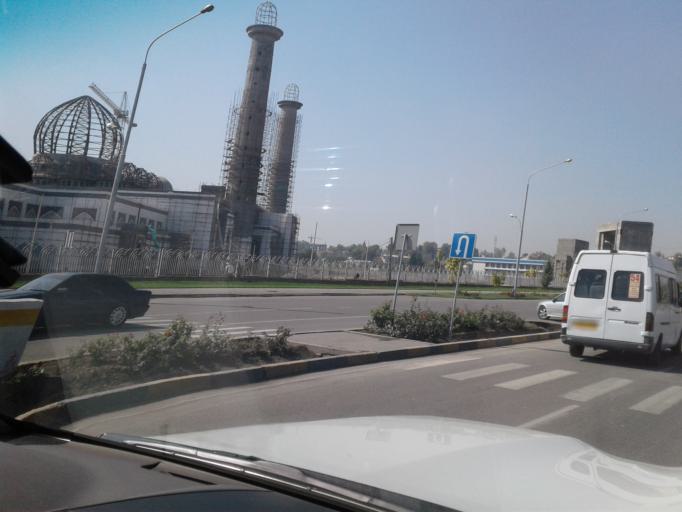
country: TJ
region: Dushanbe
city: Dushanbe
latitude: 38.5974
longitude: 68.7645
